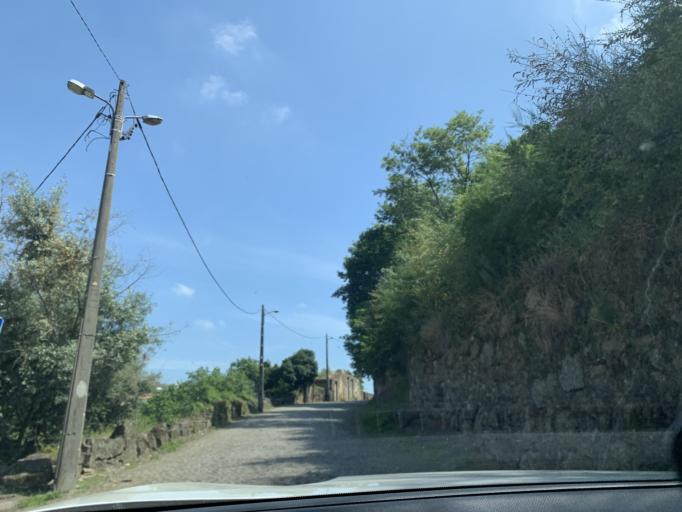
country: PT
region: Viseu
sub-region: Viseu
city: Viseu
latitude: 40.6569
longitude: -7.9327
